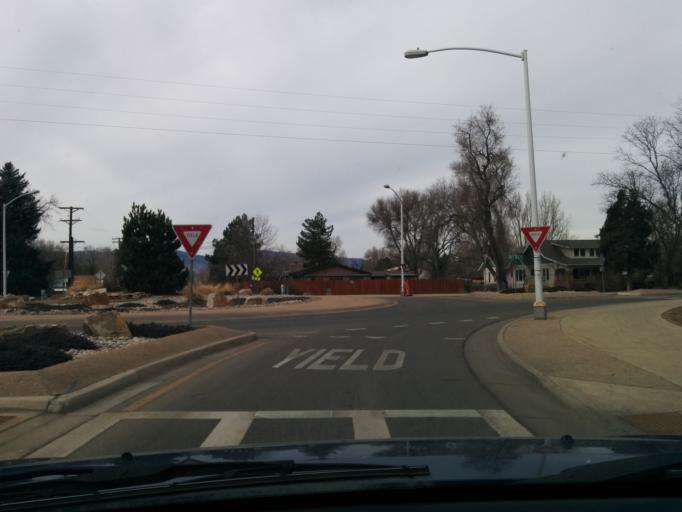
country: US
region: Colorado
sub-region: Larimer County
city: Fort Collins
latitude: 40.5965
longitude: -105.1144
